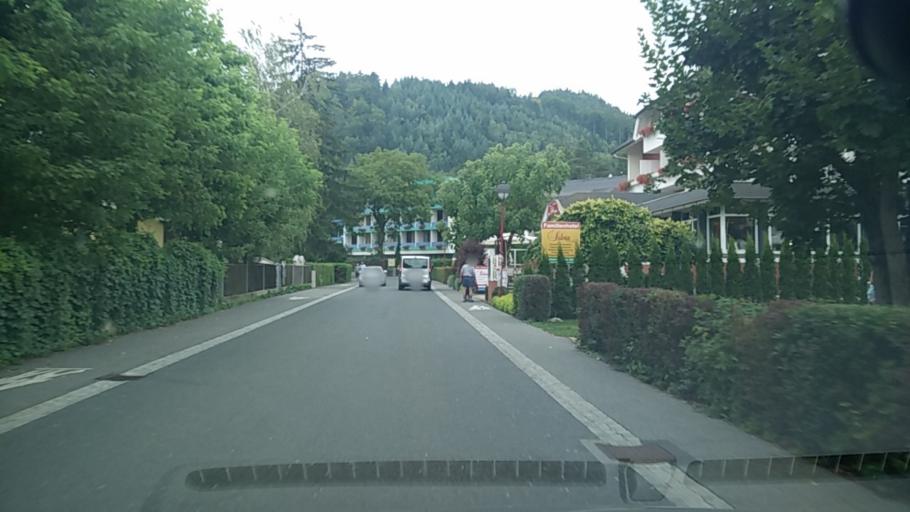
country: AT
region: Carinthia
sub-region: Politischer Bezirk Volkermarkt
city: Sittersdorf
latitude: 46.6059
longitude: 14.5729
